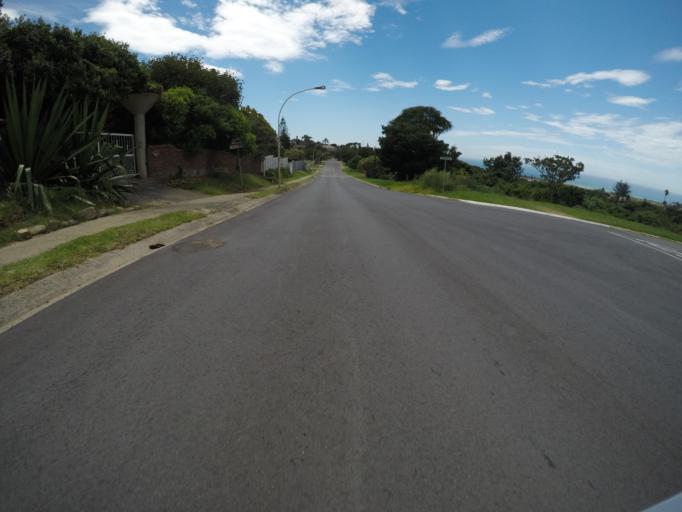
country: ZA
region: Eastern Cape
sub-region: Buffalo City Metropolitan Municipality
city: East London
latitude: -33.0373
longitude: 27.8577
